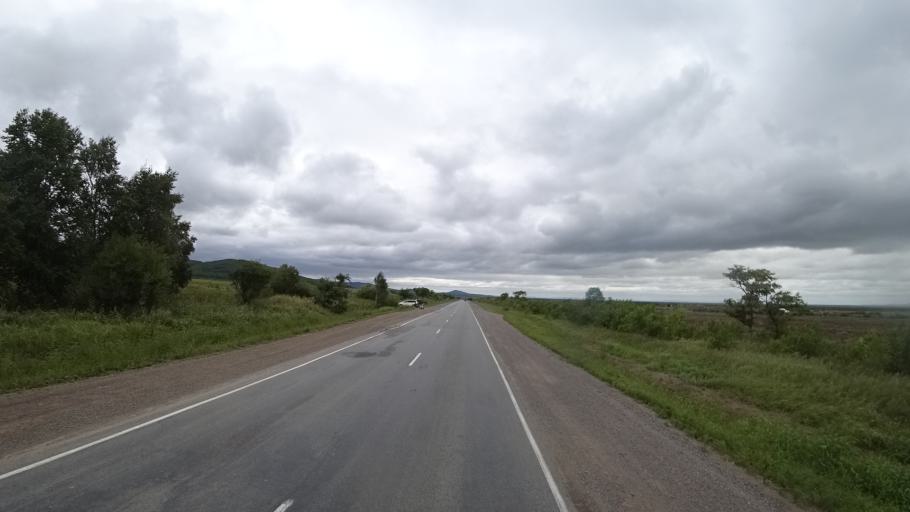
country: RU
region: Primorskiy
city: Chernigovka
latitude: 44.3140
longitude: 132.5547
